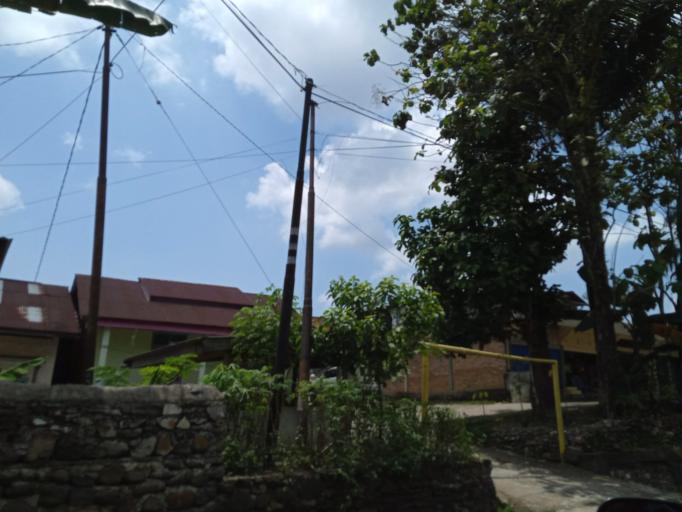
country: ID
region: Jambi
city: Bangko
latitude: -2.0850
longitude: 102.2605
